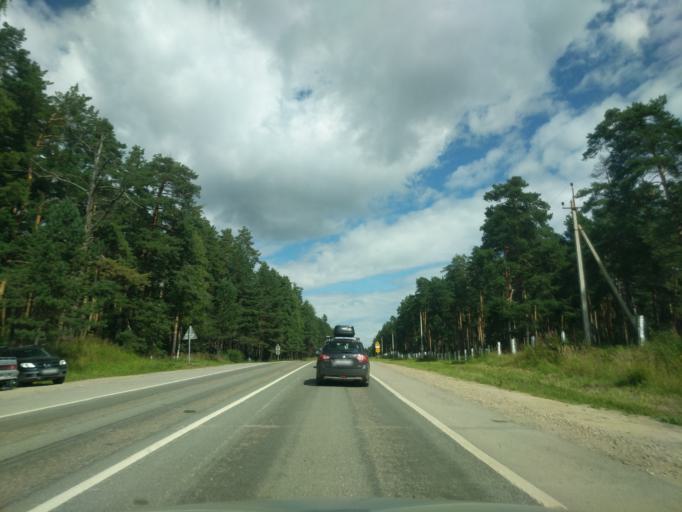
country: RU
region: Jaroslavl
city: Levashevo
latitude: 57.6724
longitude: 40.5829
